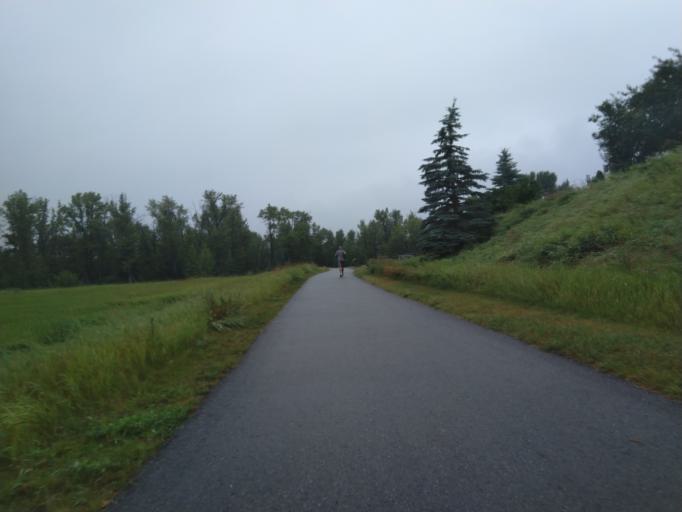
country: CA
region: Alberta
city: Cochrane
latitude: 51.1801
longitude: -114.4795
